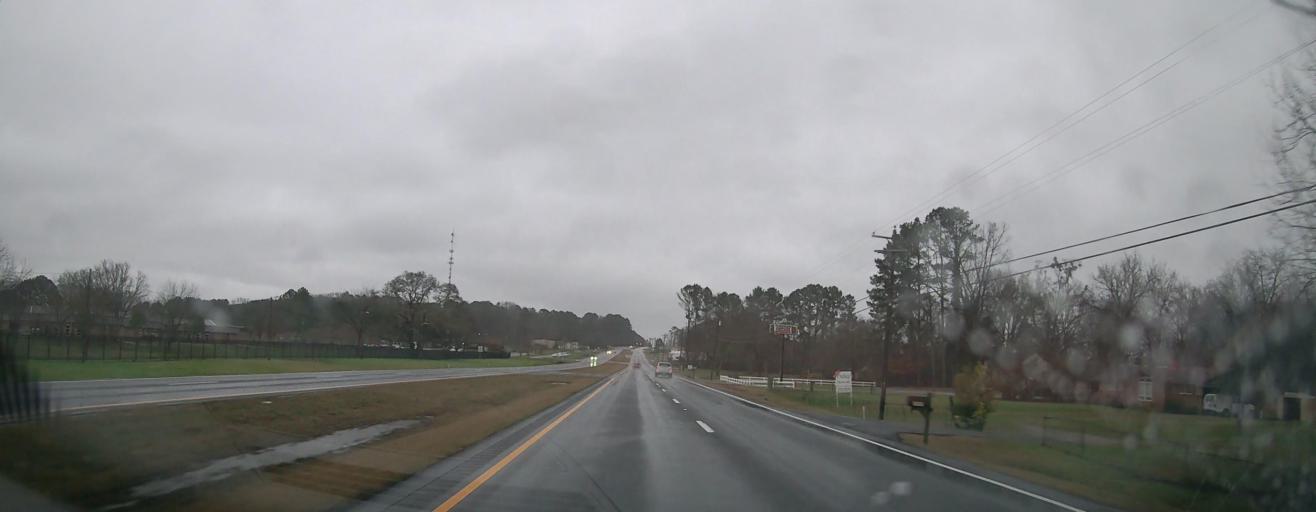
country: US
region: Alabama
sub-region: Morgan County
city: Flint City
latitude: 34.5293
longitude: -86.9728
